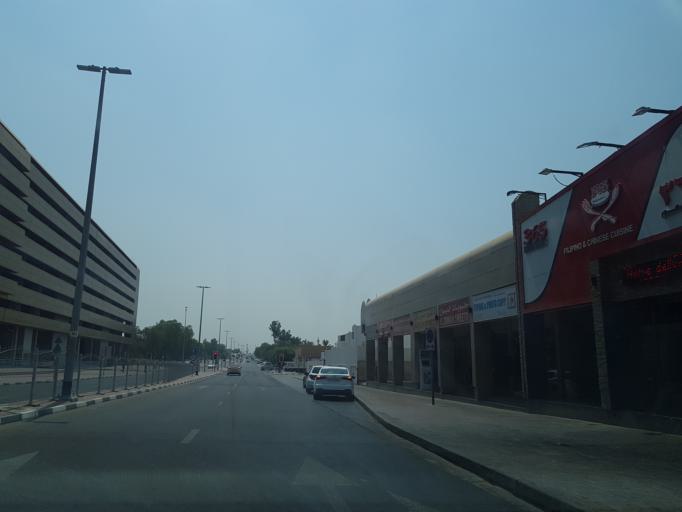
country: AE
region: Ash Shariqah
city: Sharjah
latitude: 25.2292
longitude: 55.3909
